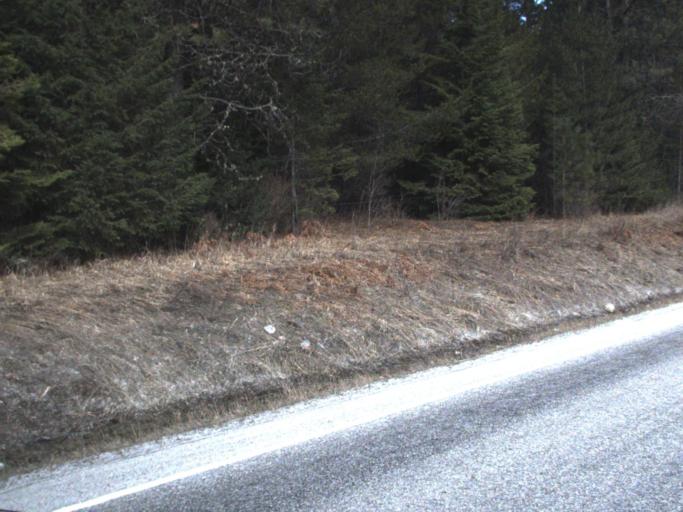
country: US
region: Washington
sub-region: Stevens County
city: Chewelah
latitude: 48.6234
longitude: -117.3671
